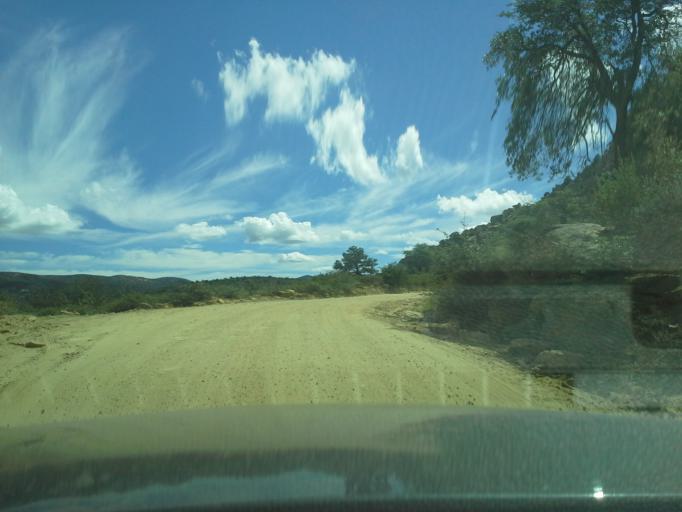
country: US
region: Arizona
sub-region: Yavapai County
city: Mayer
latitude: 34.2406
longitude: -112.3028
